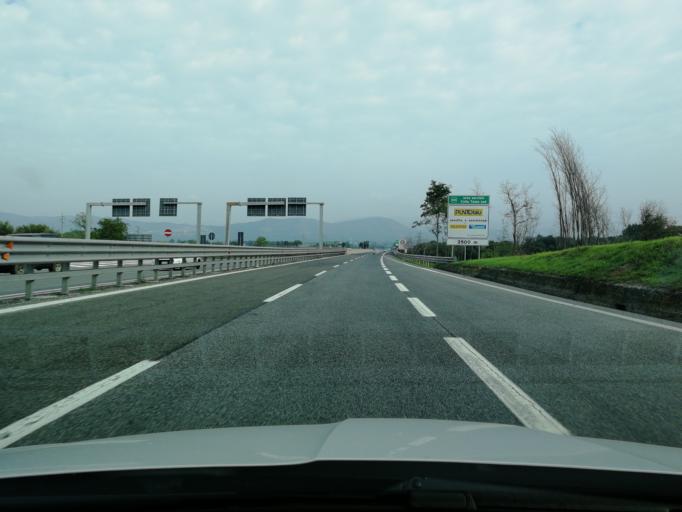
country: IT
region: Latium
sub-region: Citta metropolitana di Roma Capitale
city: Bagni di Tivoli
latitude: 41.9262
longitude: 12.7082
